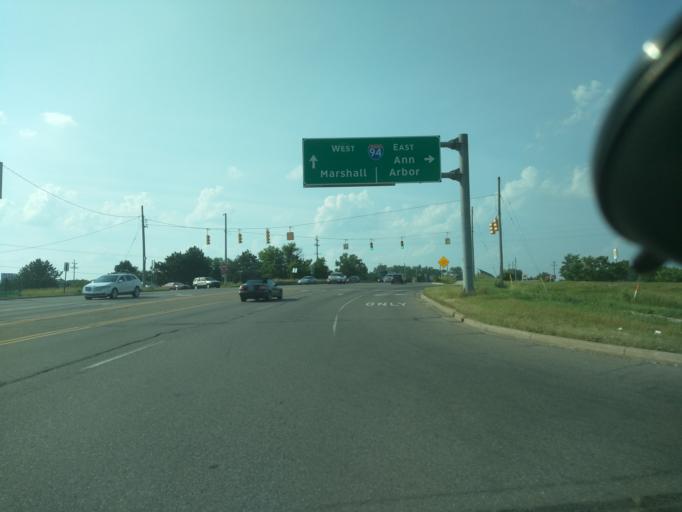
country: US
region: Michigan
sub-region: Jackson County
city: Jackson
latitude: 42.2677
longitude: -84.4526
